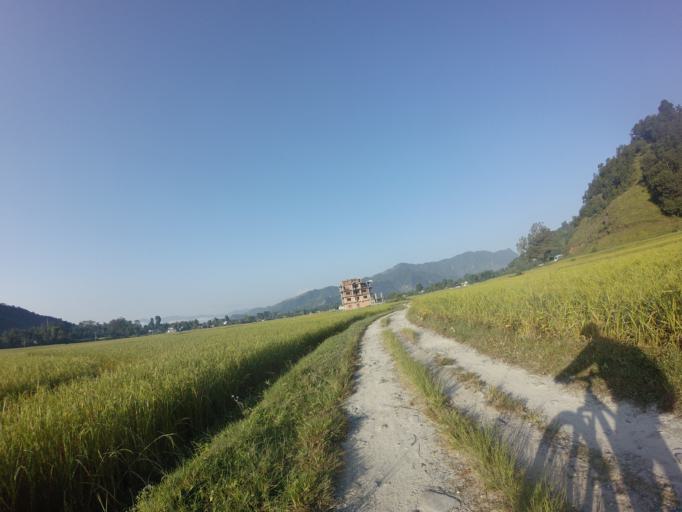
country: NP
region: Western Region
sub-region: Gandaki Zone
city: Pokhara
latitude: 28.2503
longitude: 84.0018
